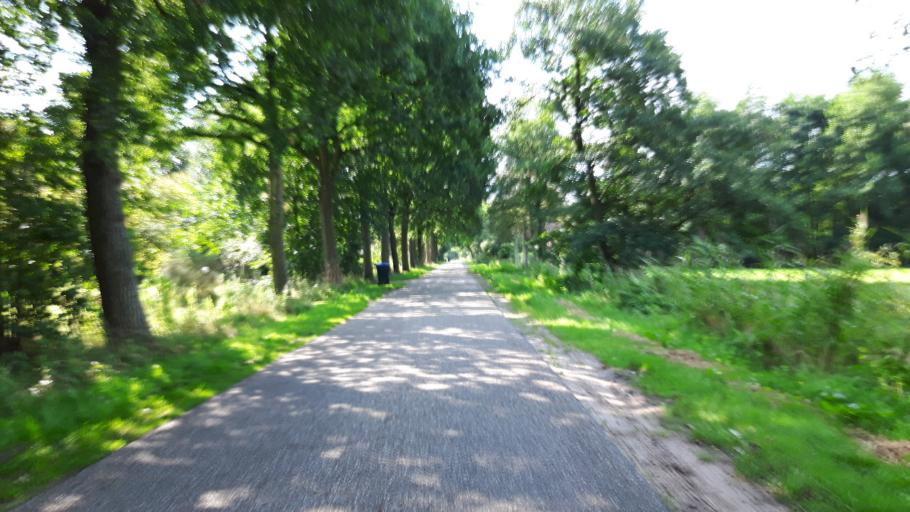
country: NL
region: Groningen
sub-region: Gemeente Leek
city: Leek
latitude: 53.1265
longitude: 6.4556
